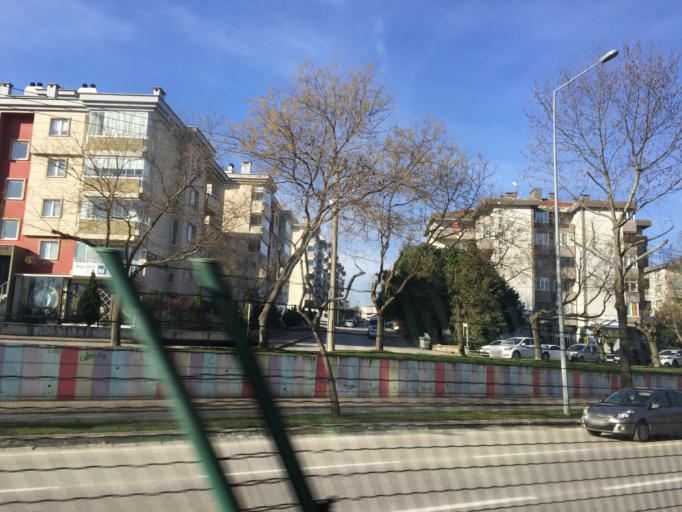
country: TR
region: Bursa
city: Yildirim
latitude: 40.2259
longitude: 28.9911
